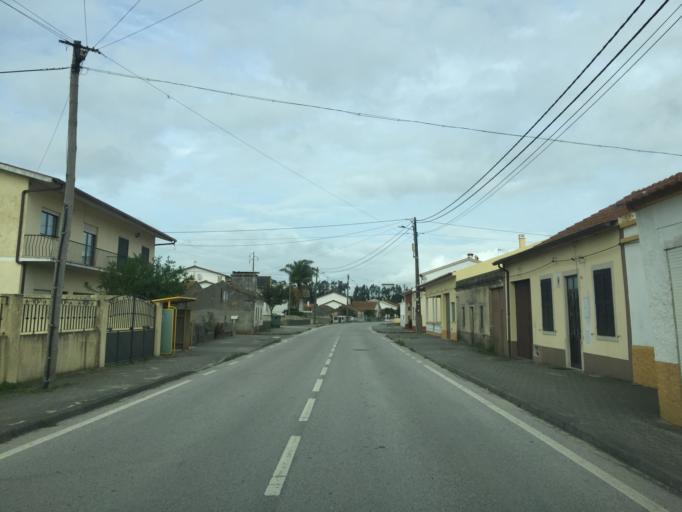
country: PT
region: Coimbra
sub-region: Figueira da Foz
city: Lavos
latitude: 40.0372
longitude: -8.8201
